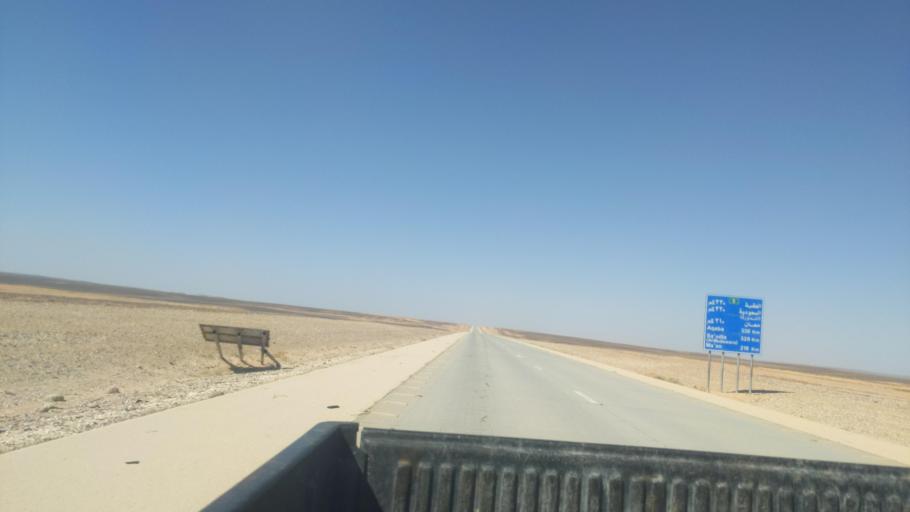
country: JO
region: Amman
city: Al Azraq ash Shamali
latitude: 31.4414
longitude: 36.7547
